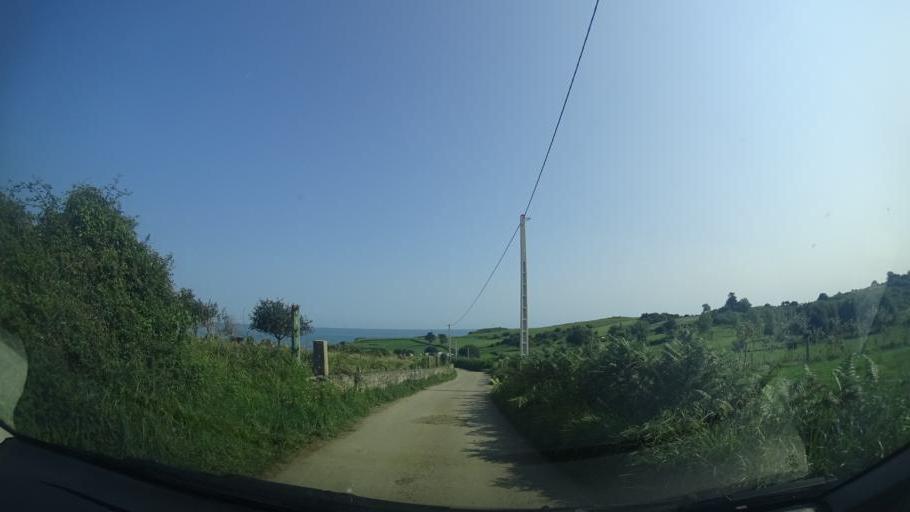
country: ES
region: Asturias
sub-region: Province of Asturias
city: Colunga
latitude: 43.4704
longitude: -5.2042
